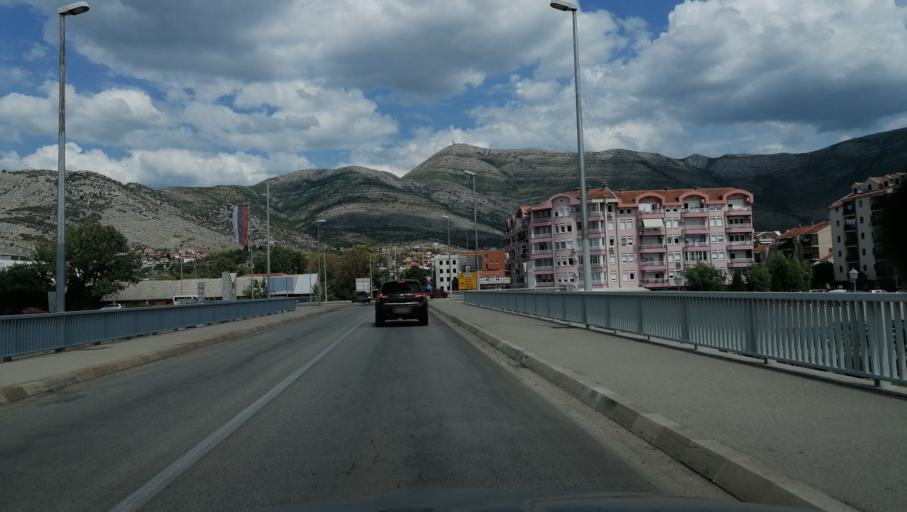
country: BA
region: Republika Srpska
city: Trebinje
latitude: 42.7045
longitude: 18.3430
